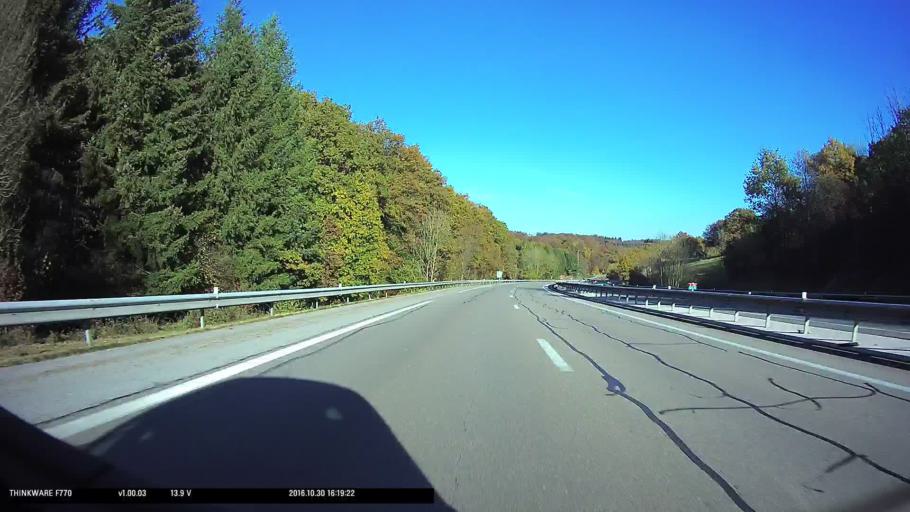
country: FR
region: Franche-Comte
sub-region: Departement du Doubs
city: Clerval
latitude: 47.4075
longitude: 6.4766
